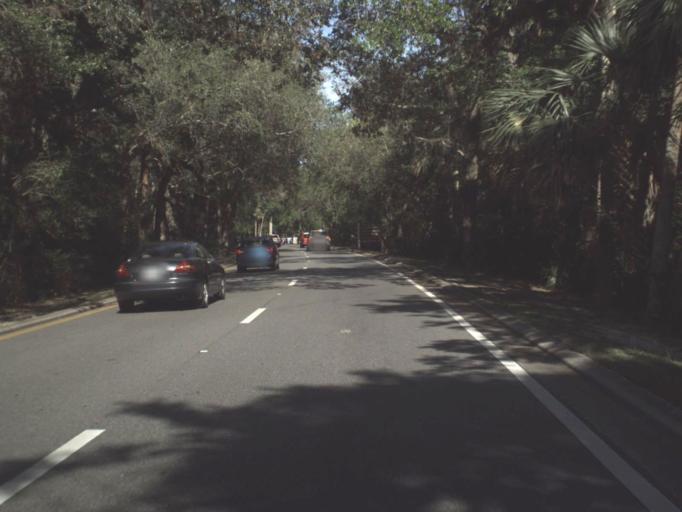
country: US
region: Florida
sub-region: Flagler County
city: Palm Coast
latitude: 29.5566
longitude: -81.1998
